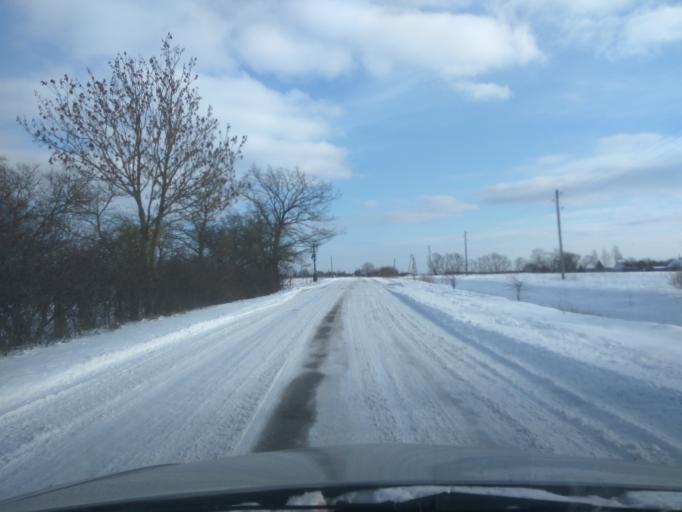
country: LV
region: Ventspils Rajons
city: Piltene
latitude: 57.3319
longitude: 21.6539
